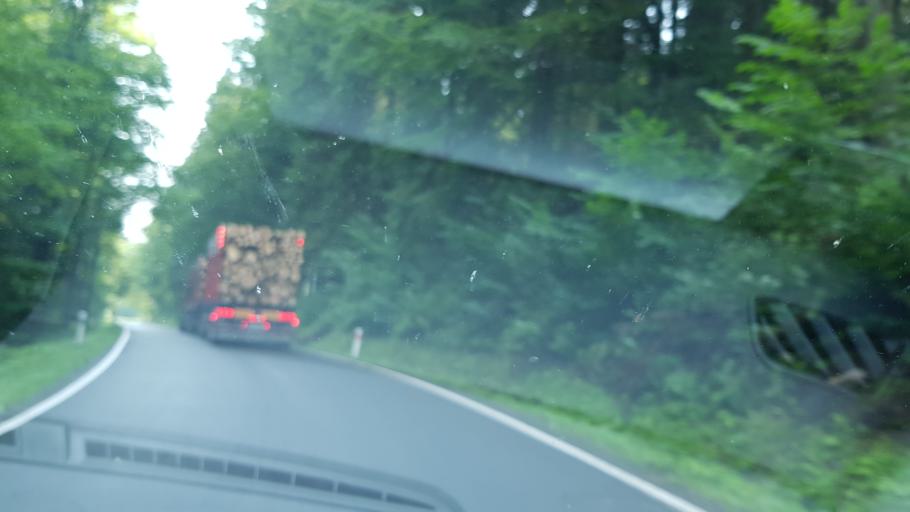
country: CZ
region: Olomoucky
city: Mikulovice
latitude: 50.2351
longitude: 17.3326
